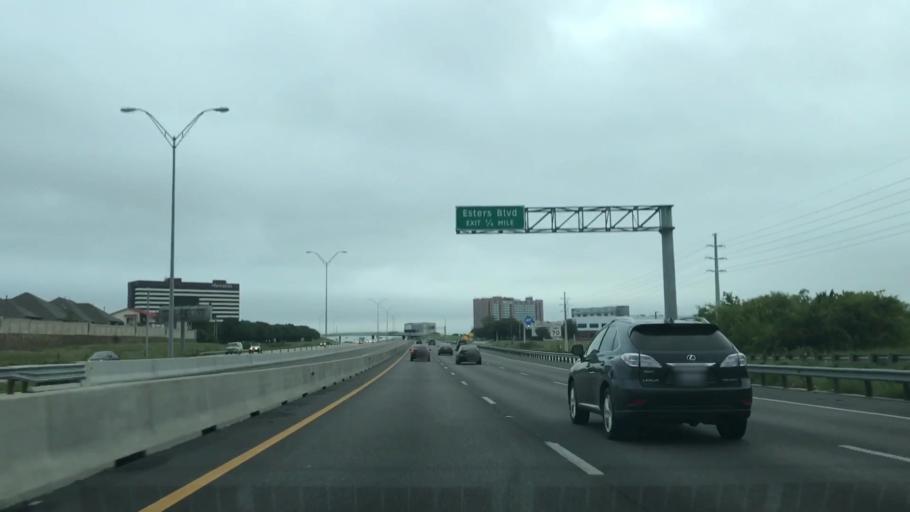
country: US
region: Texas
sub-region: Dallas County
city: Coppell
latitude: 32.9115
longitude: -97.0014
